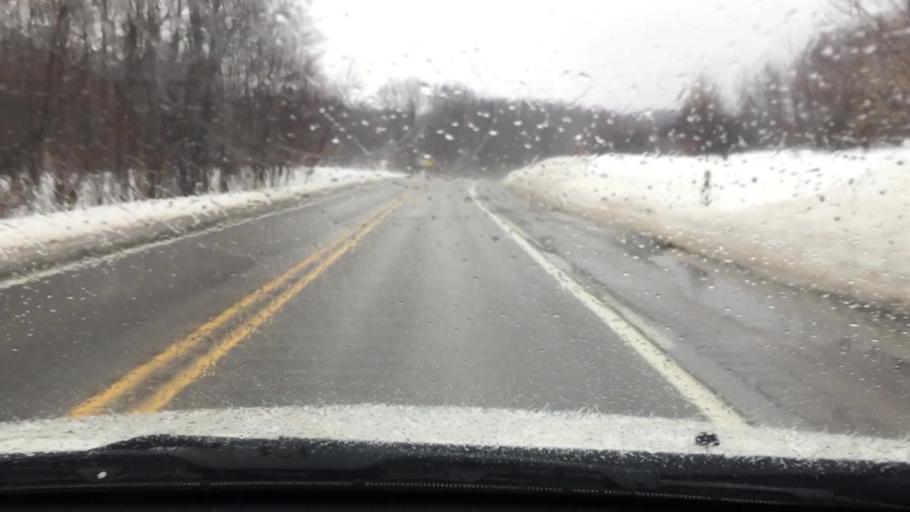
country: US
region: Michigan
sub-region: Charlevoix County
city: East Jordan
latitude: 45.2107
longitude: -85.1700
